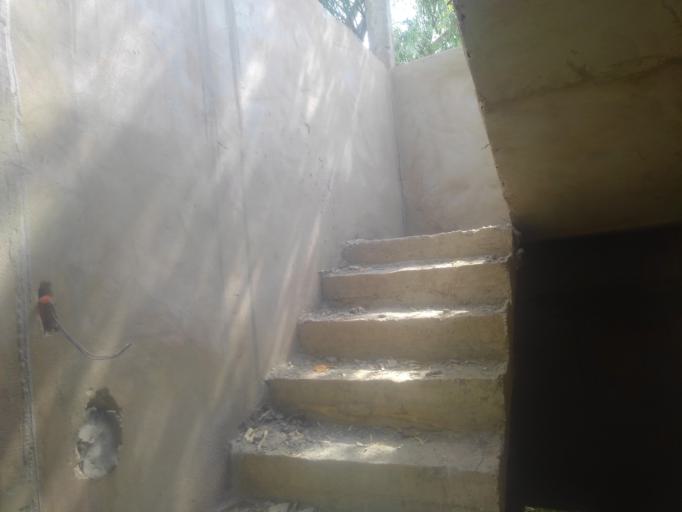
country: SN
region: Matam
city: Matam
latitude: 15.6491
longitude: -13.2508
